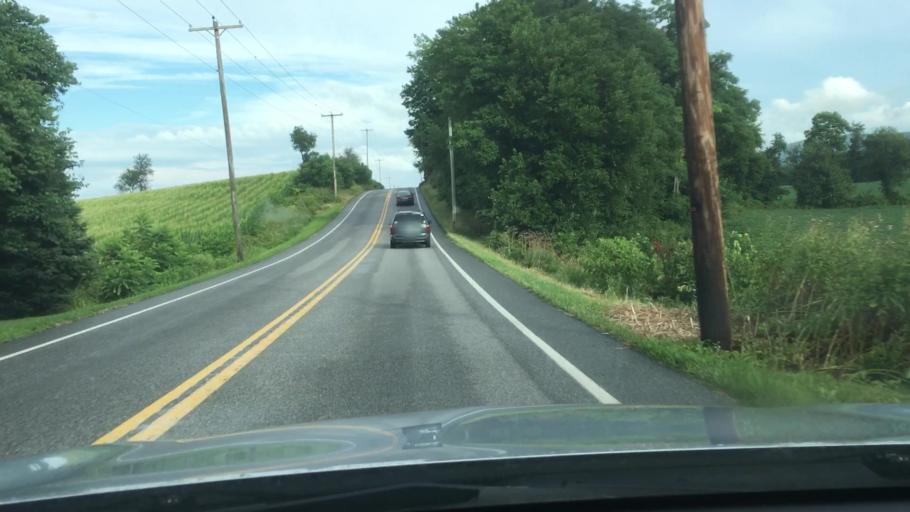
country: US
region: Pennsylvania
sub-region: Cumberland County
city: Boiling Springs
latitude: 40.1663
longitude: -77.1069
